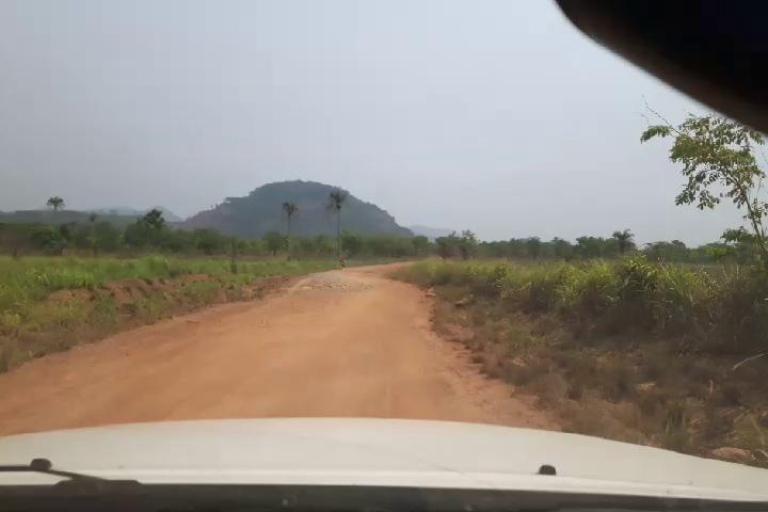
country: SL
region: Northern Province
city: Bumbuna
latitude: 8.8918
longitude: -11.8181
